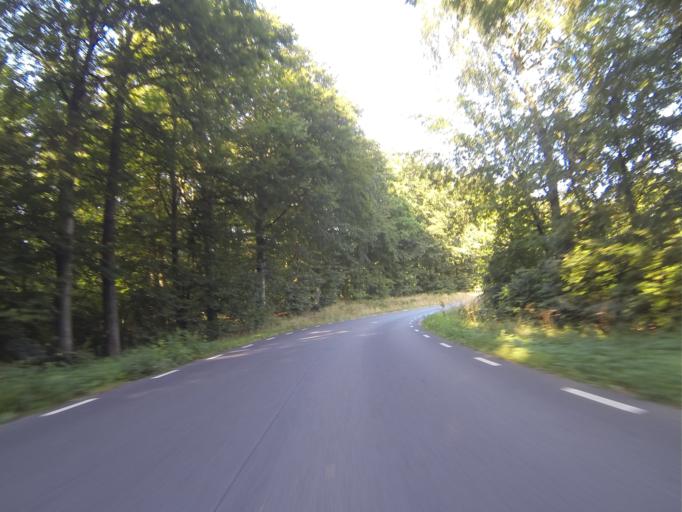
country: SE
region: Skane
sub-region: Lunds Kommun
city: Genarp
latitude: 55.5905
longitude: 13.3566
